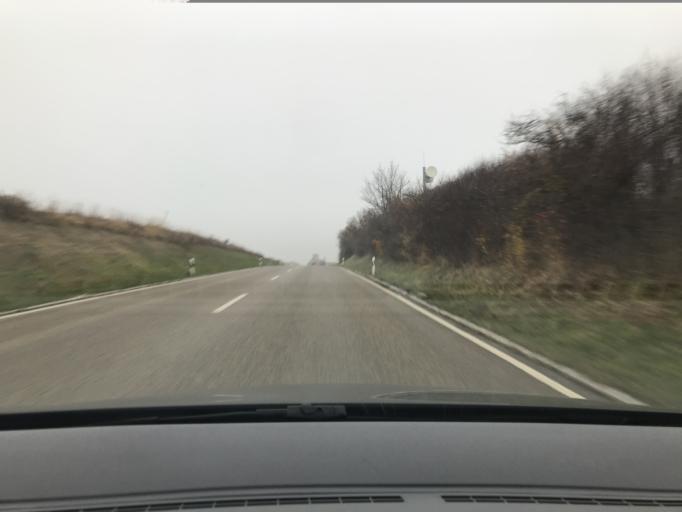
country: DE
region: Bavaria
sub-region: Swabia
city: Marktoffingen
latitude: 48.9322
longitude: 10.4620
